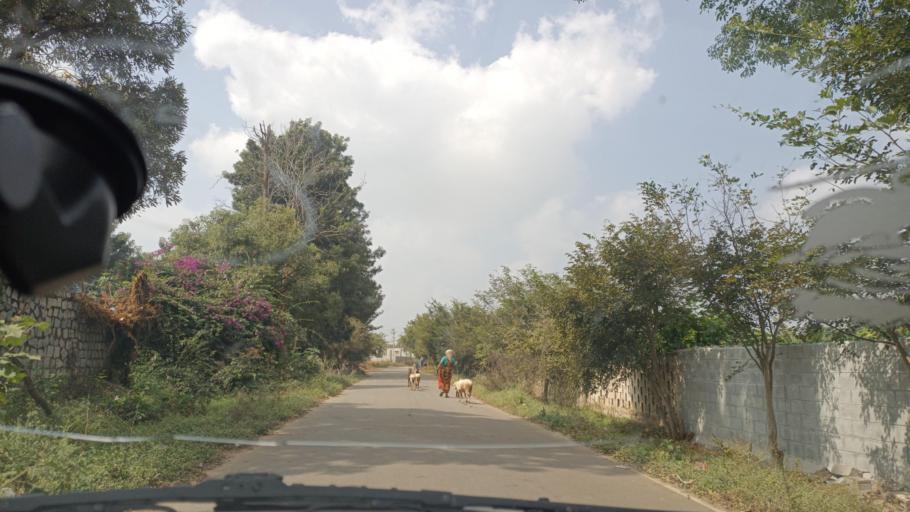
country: IN
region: Karnataka
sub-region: Bangalore Urban
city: Yelahanka
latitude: 13.1492
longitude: 77.6368
